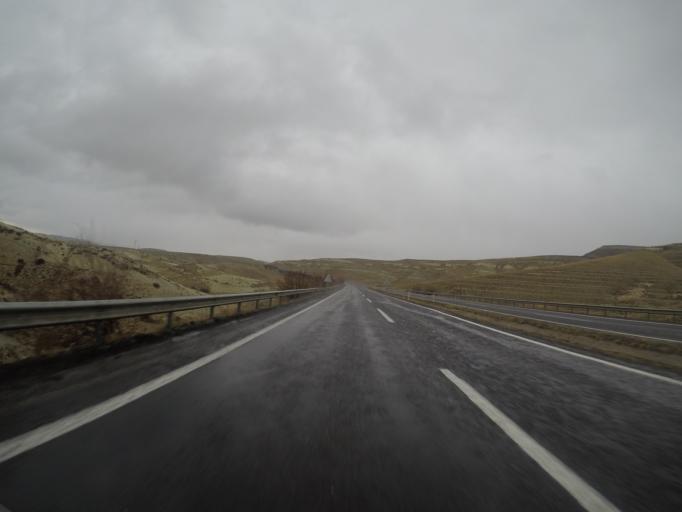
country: TR
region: Nevsehir
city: Urgub
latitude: 38.7387
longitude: 34.9932
